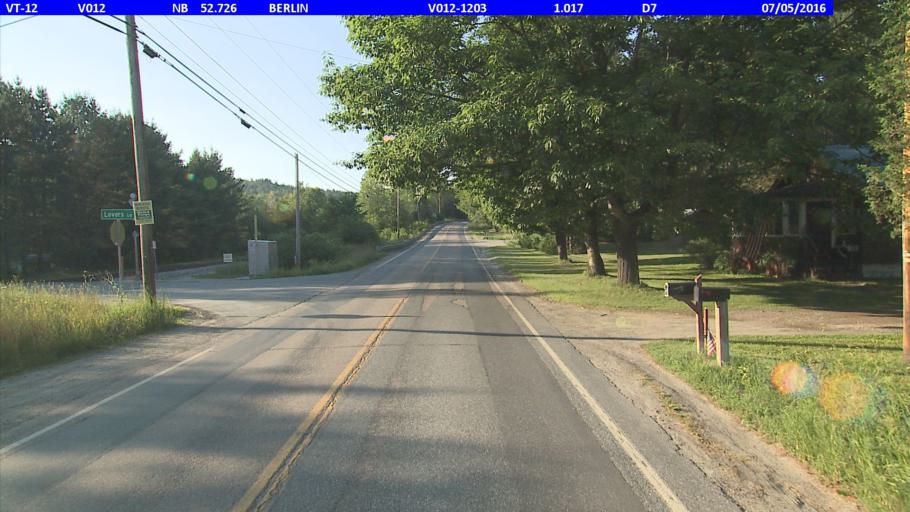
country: US
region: Vermont
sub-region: Washington County
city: Northfield
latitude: 44.1878
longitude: -72.6397
